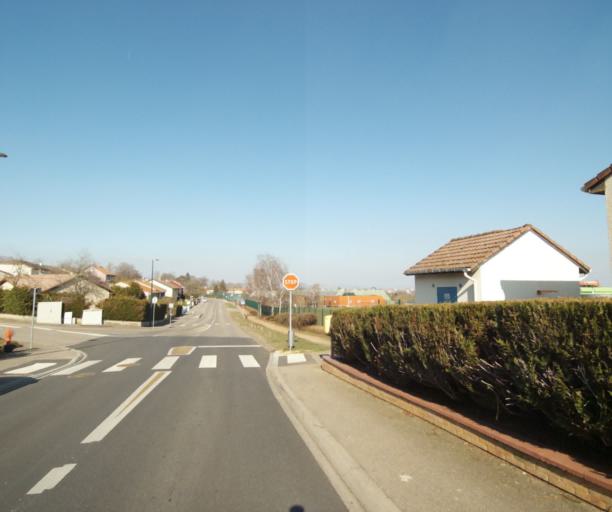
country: FR
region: Lorraine
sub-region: Departement de Meurthe-et-Moselle
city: Vandoeuvre-les-Nancy
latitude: 48.6414
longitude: 6.1769
